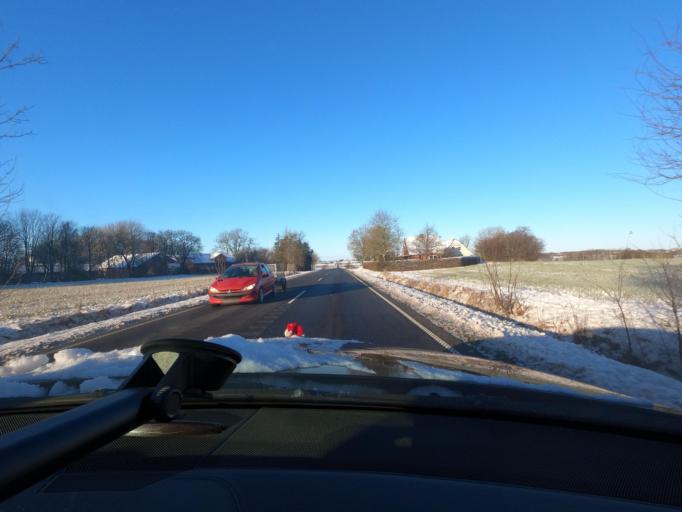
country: DK
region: South Denmark
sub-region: Tonder Kommune
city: Toftlund
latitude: 55.1649
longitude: 9.0769
